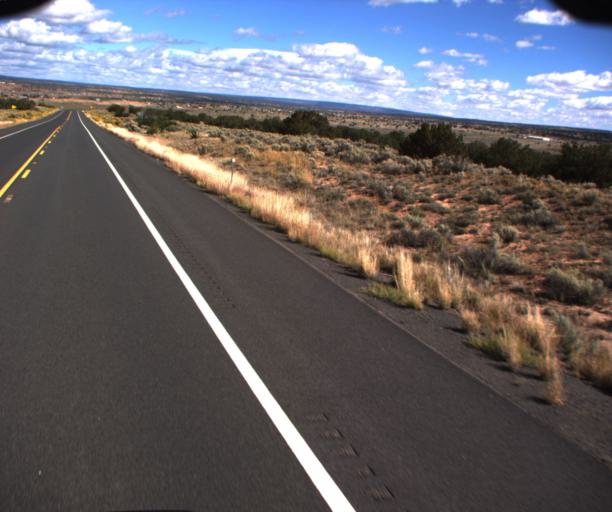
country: US
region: Arizona
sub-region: Apache County
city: Houck
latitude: 35.1839
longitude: -109.3368
